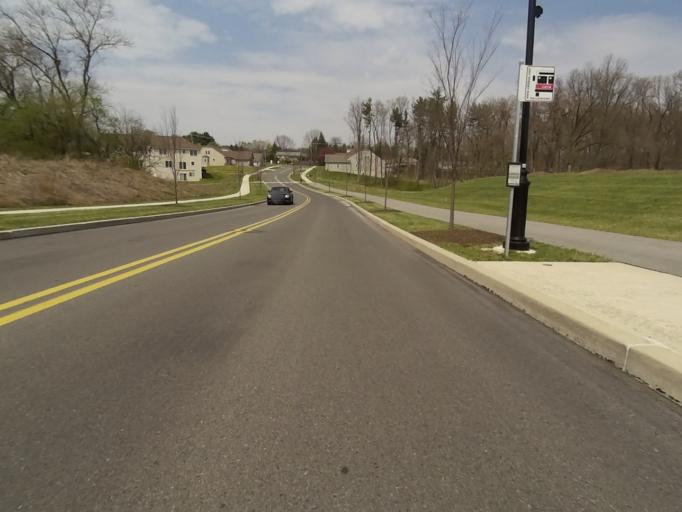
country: US
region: Pennsylvania
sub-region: Centre County
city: Park Forest Village
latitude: 40.7906
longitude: -77.8978
